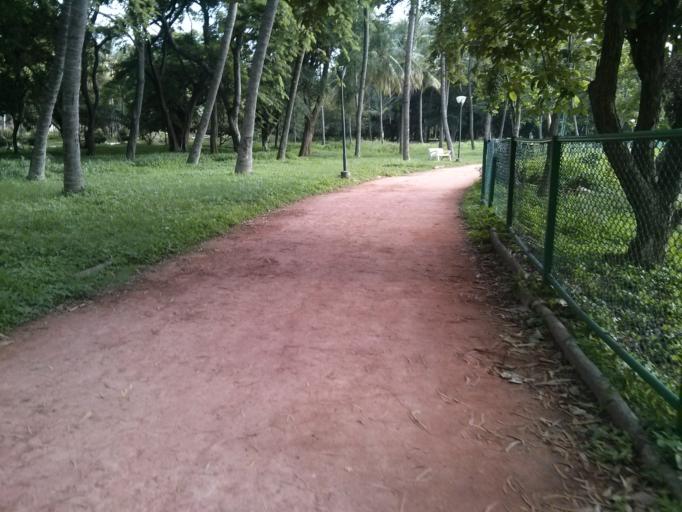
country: IN
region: Karnataka
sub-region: Bangalore Urban
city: Bangalore
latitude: 12.9441
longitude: 77.5812
